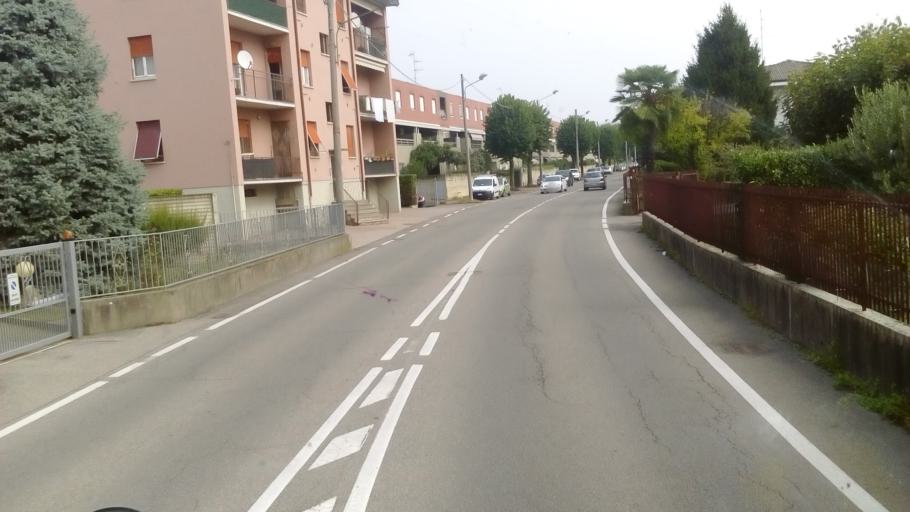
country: IT
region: Lombardy
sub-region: Provincia di Como
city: Rovellasca
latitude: 45.6710
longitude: 9.0457
